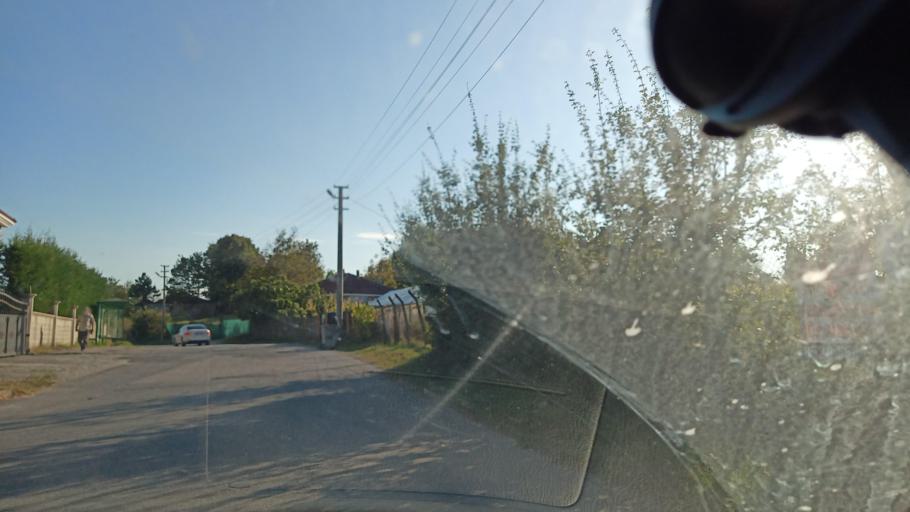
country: TR
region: Sakarya
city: Kazimpasa
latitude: 40.8567
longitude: 30.2852
